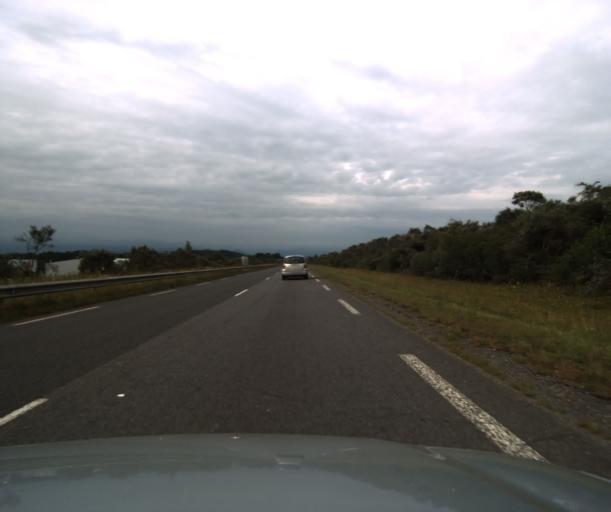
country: FR
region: Midi-Pyrenees
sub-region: Departement des Hautes-Pyrenees
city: Juillan
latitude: 43.2036
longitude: 0.0089
